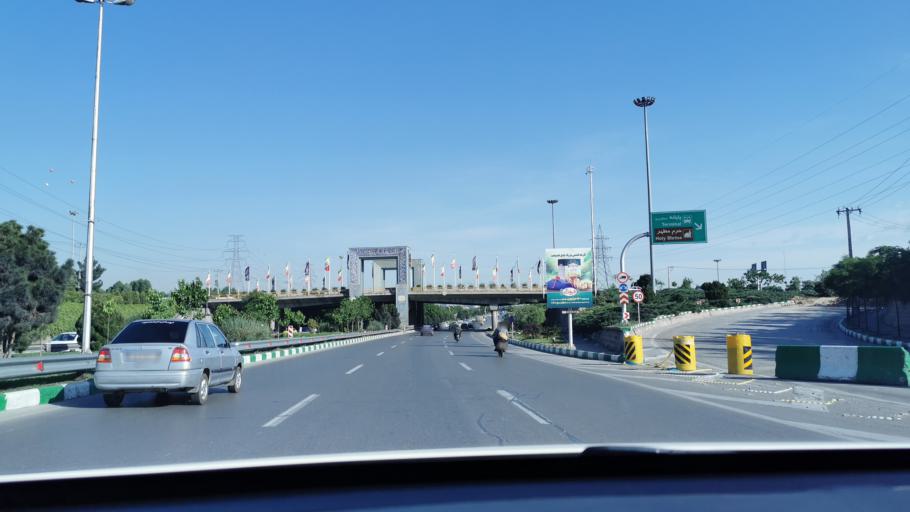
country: IR
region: Razavi Khorasan
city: Mashhad
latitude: 36.2619
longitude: 59.5843
